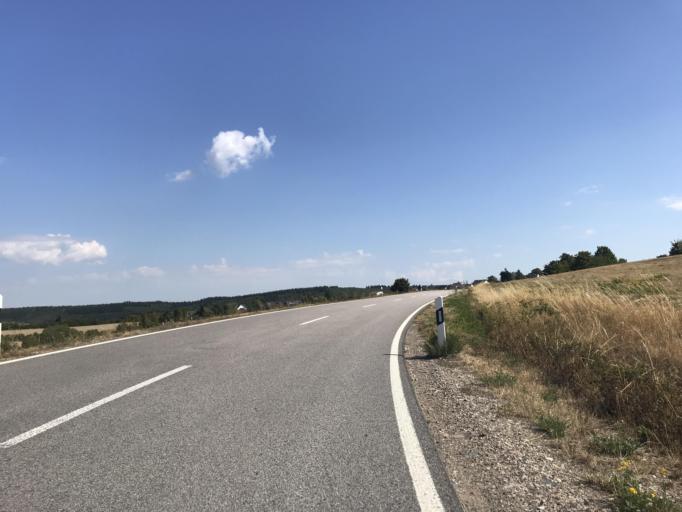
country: DE
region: Rheinland-Pfalz
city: Trechtingshausen
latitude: 50.0510
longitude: 7.8848
